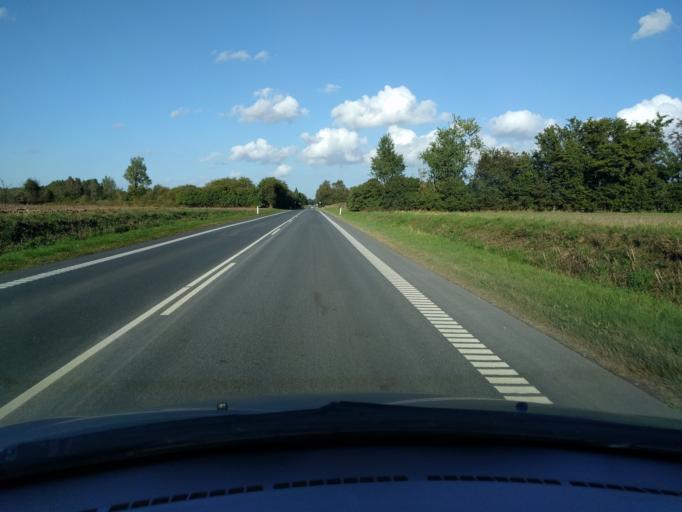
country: DK
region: South Denmark
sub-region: Odense Kommune
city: Bellinge
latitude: 55.3100
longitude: 10.2662
